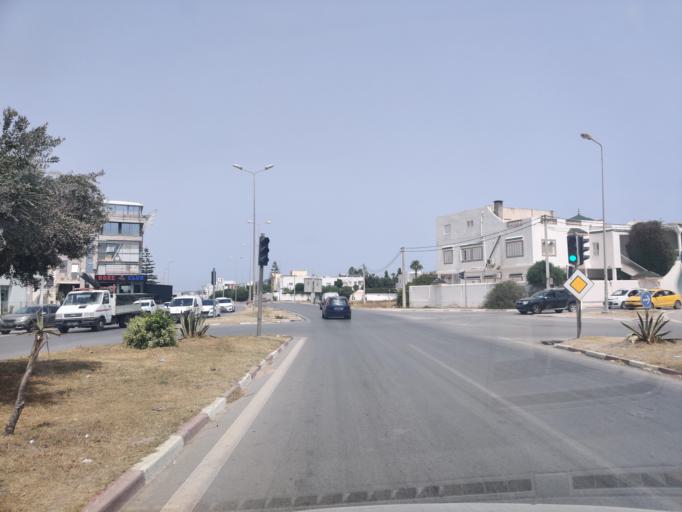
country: TN
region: Tunis
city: Carthage
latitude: 36.8643
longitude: 10.3159
